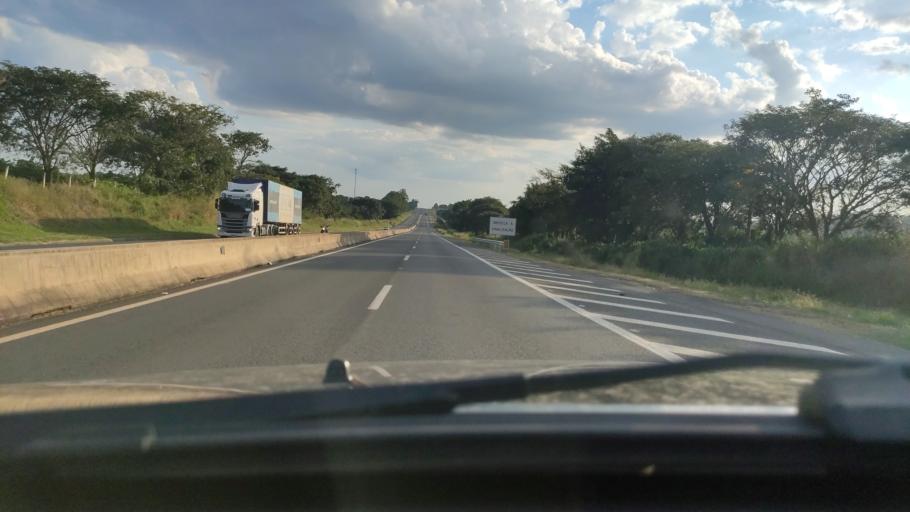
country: BR
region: Sao Paulo
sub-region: Artur Nogueira
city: Artur Nogueira
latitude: -22.4580
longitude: -47.0966
